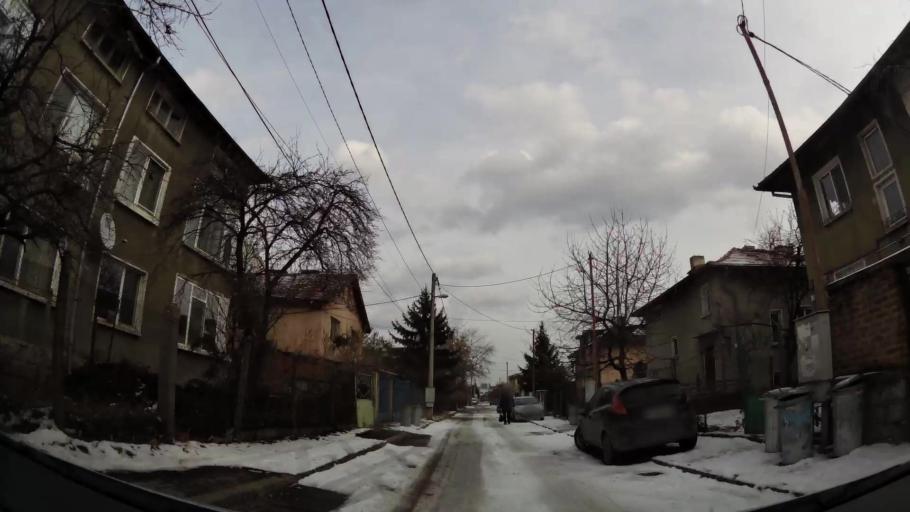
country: BG
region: Sofia-Capital
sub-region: Stolichna Obshtina
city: Sofia
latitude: 42.7031
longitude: 23.3828
